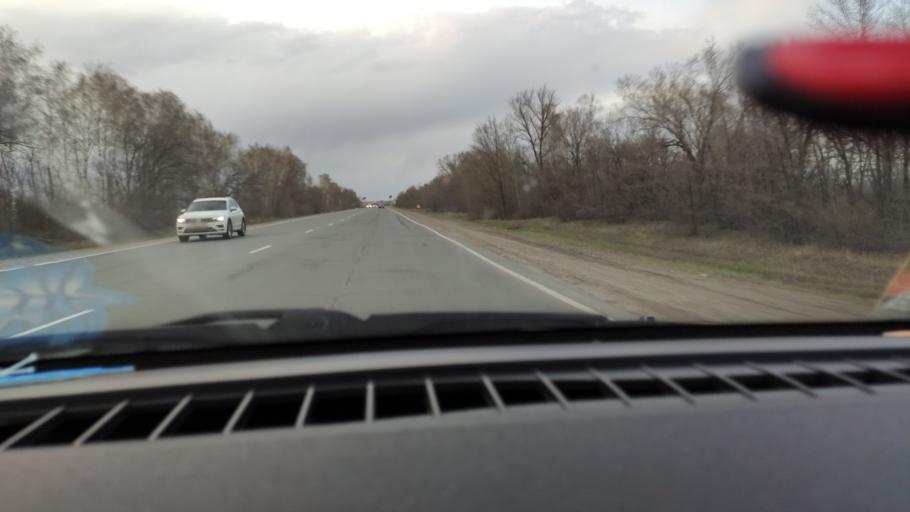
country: RU
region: Saratov
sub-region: Saratovskiy Rayon
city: Saratov
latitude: 51.7050
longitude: 46.0136
